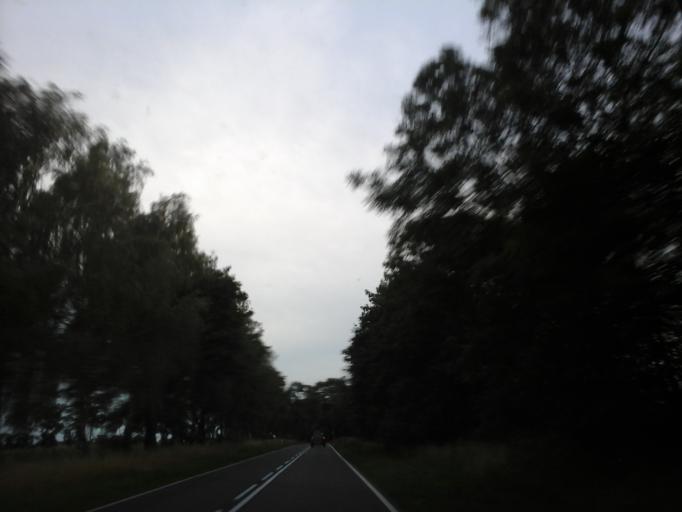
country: PL
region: West Pomeranian Voivodeship
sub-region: Powiat stargardzki
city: Stargard Szczecinski
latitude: 53.3636
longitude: 15.0660
